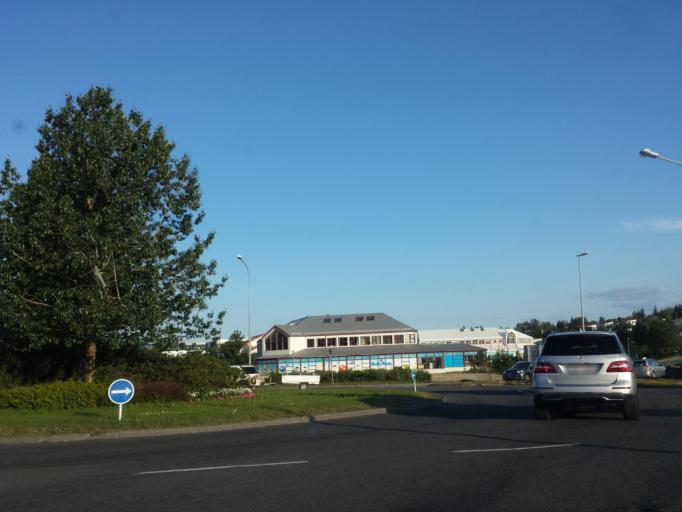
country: IS
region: Capital Region
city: Reykjavik
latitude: 64.1304
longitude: -21.8634
